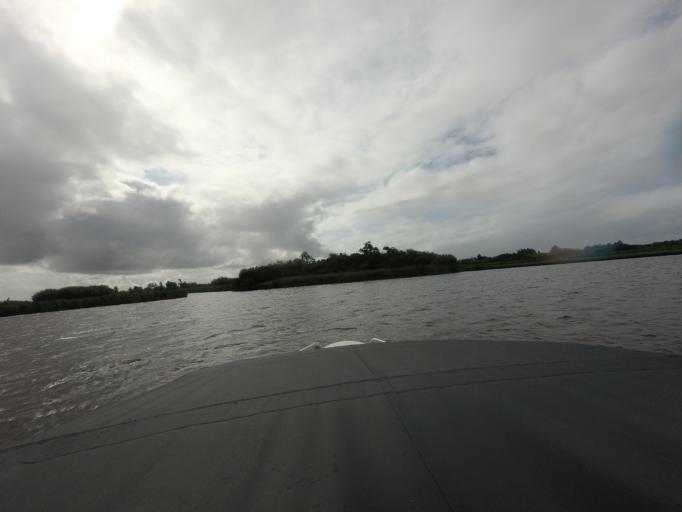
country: NL
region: Friesland
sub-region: Gemeente Boarnsterhim
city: Warten
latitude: 53.1325
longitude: 5.8964
